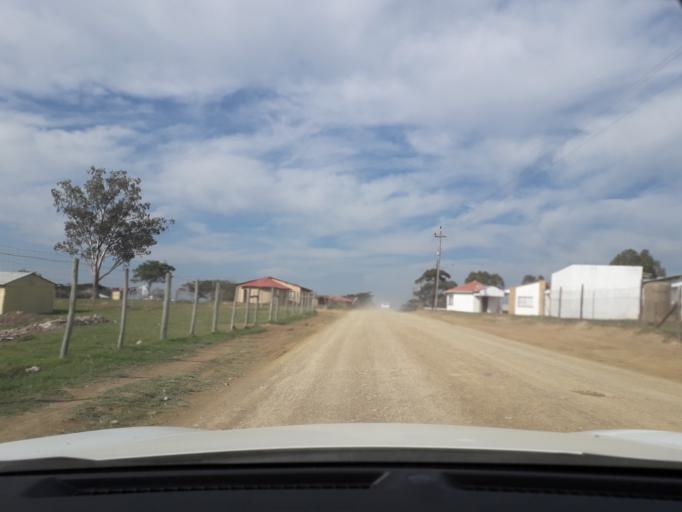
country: ZA
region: Eastern Cape
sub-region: Buffalo City Metropolitan Municipality
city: Bhisho
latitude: -33.0014
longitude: 27.3322
